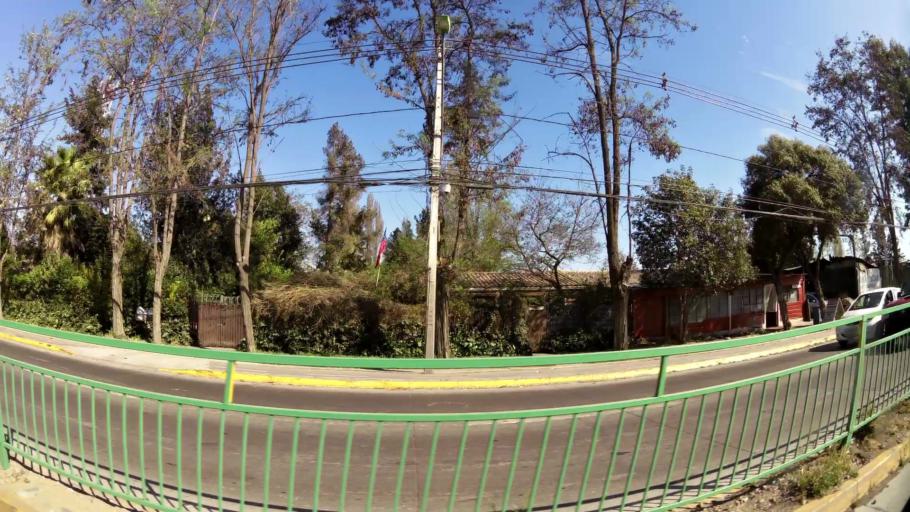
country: CL
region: Santiago Metropolitan
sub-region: Provincia de Santiago
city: La Pintana
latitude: -33.5851
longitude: -70.6243
